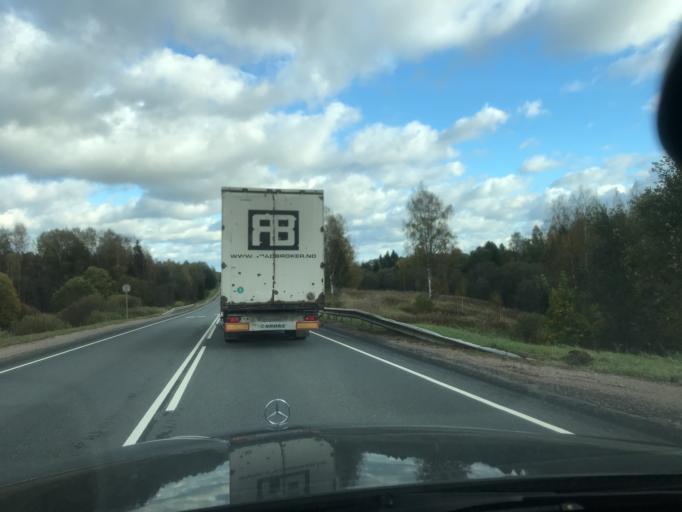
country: RU
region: Pskov
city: Novosokol'niki
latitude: 56.3433
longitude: 29.9499
